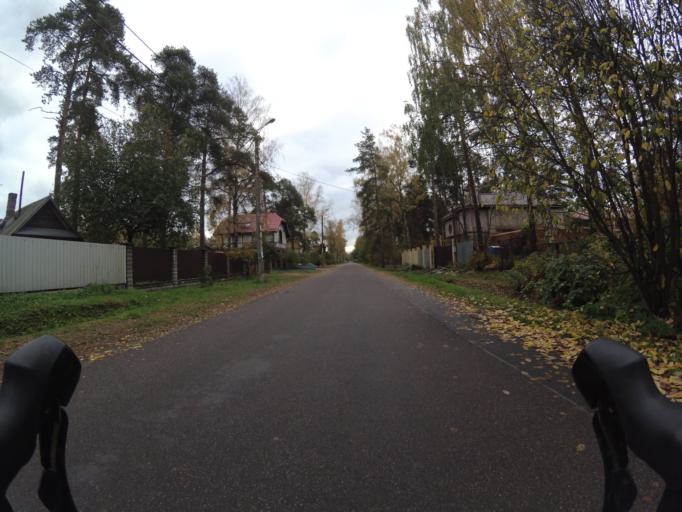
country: RU
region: St.-Petersburg
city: Lakhtinskiy
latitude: 60.0012
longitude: 30.1314
